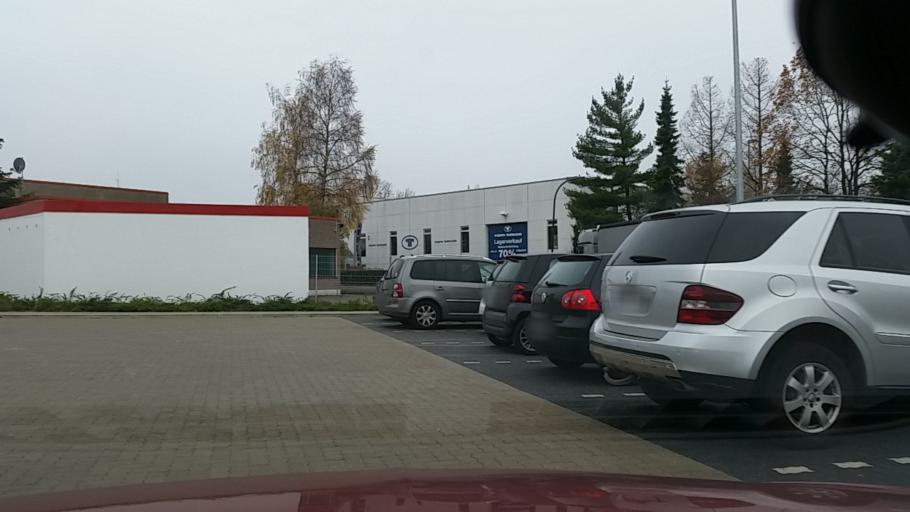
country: DE
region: Schleswig-Holstein
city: Oststeinbek
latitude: 53.5495
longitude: 10.1543
